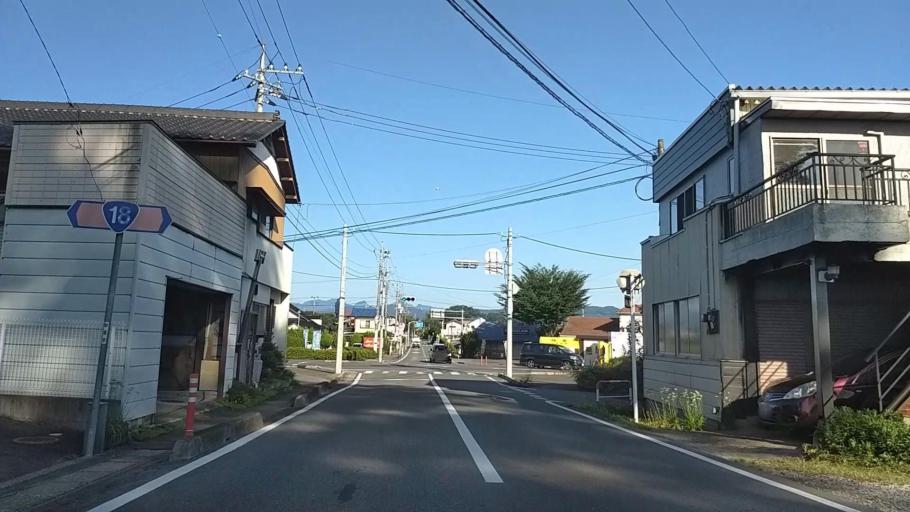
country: JP
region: Gunma
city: Annaka
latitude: 36.3247
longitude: 138.8837
